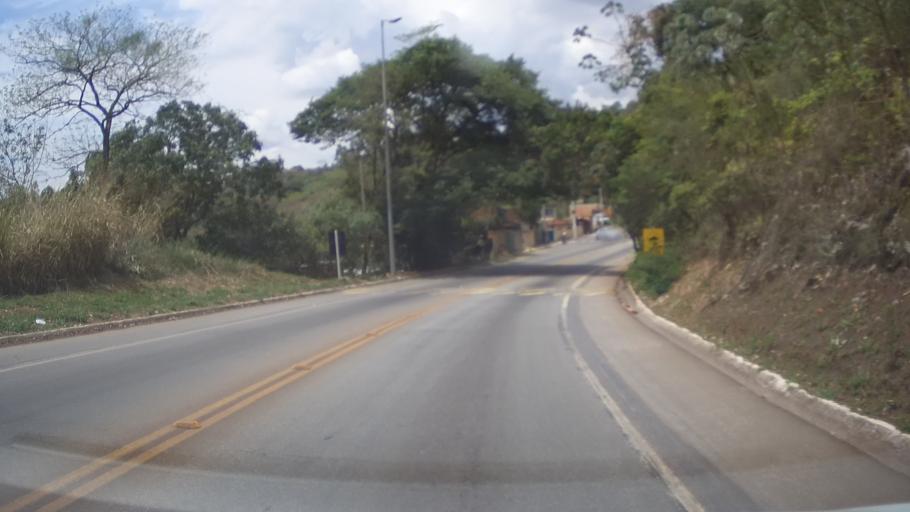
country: BR
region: Minas Gerais
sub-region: Nova Lima
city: Nova Lima
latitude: -20.0038
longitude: -43.8587
